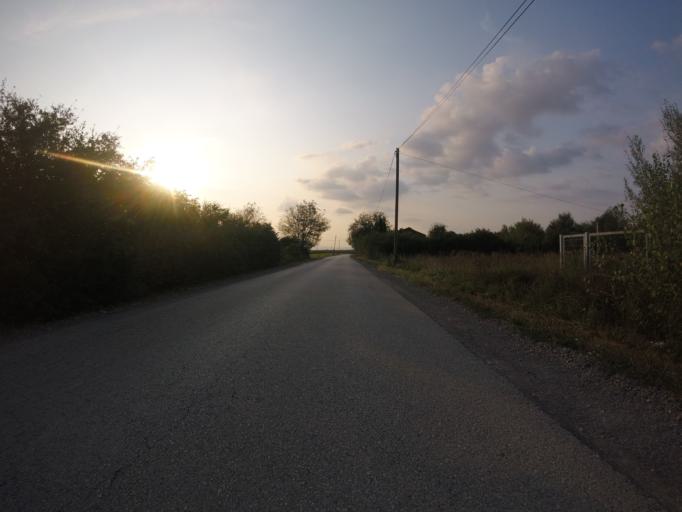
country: HR
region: Zagrebacka
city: Micevec
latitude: 45.7522
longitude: 16.1294
